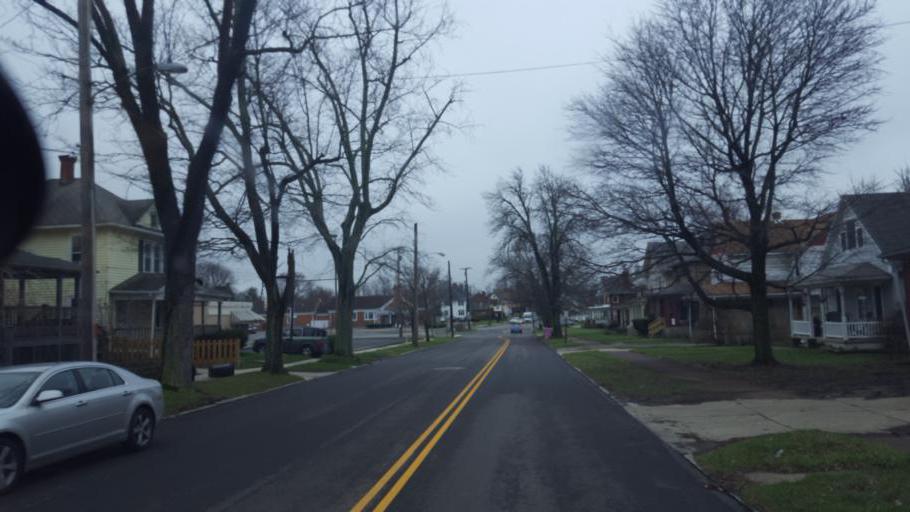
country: US
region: Ohio
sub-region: Richland County
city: Mansfield
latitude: 40.7561
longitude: -82.5341
